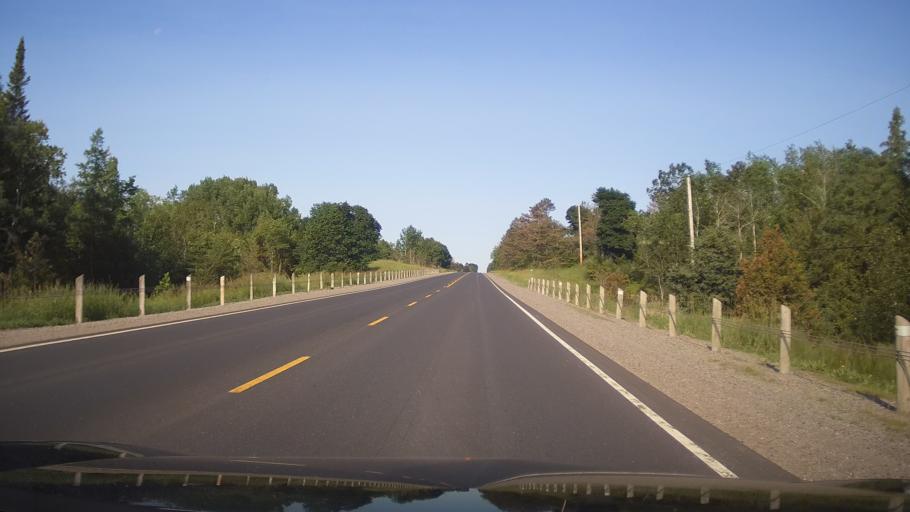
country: CA
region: Ontario
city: Belleville
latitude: 44.5257
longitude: -77.4153
